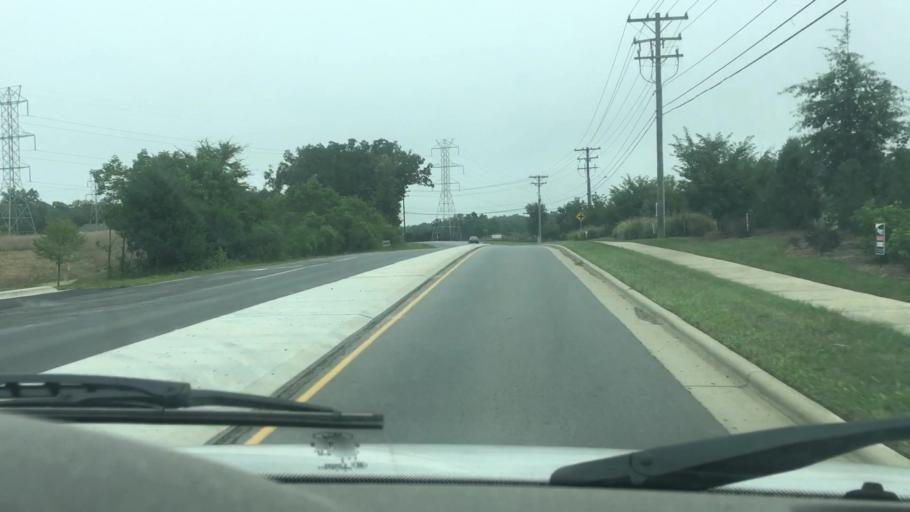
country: US
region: North Carolina
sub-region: Mecklenburg County
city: Huntersville
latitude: 35.4039
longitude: -80.7580
